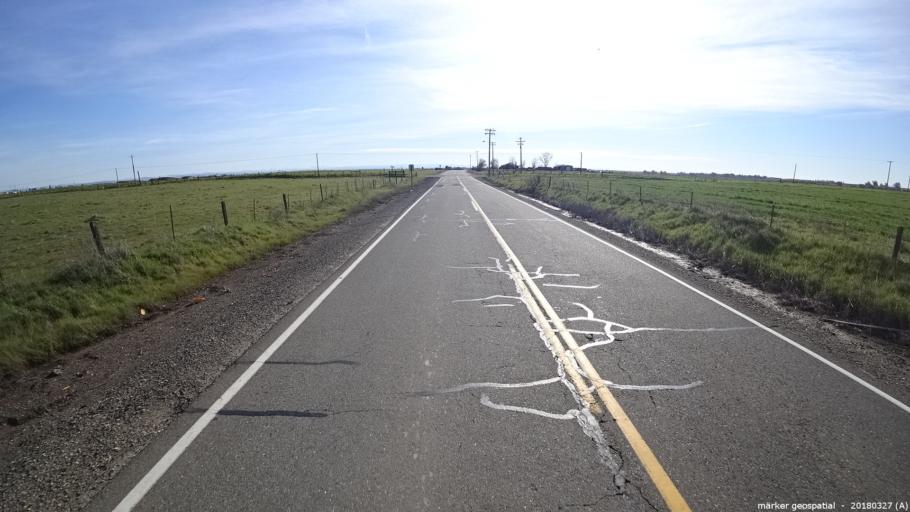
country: US
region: California
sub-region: Sacramento County
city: Wilton
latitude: 38.4968
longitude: -121.2623
